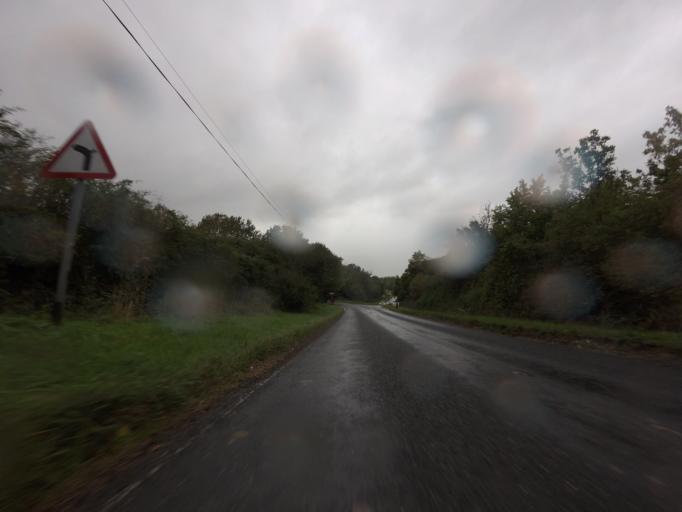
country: GB
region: England
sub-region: Cambridgeshire
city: Wimpole
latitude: 52.1857
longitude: -0.0587
